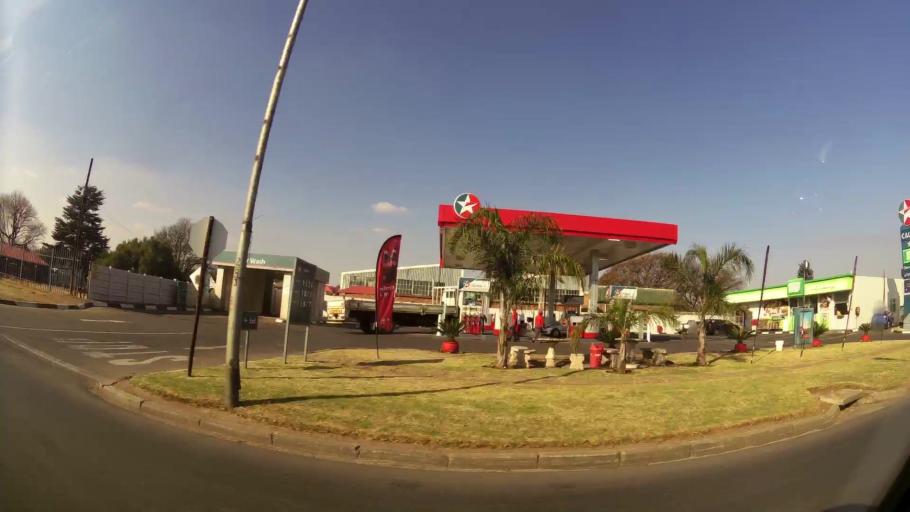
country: ZA
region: Gauteng
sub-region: Ekurhuleni Metropolitan Municipality
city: Brakpan
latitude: -26.2247
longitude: 28.3596
